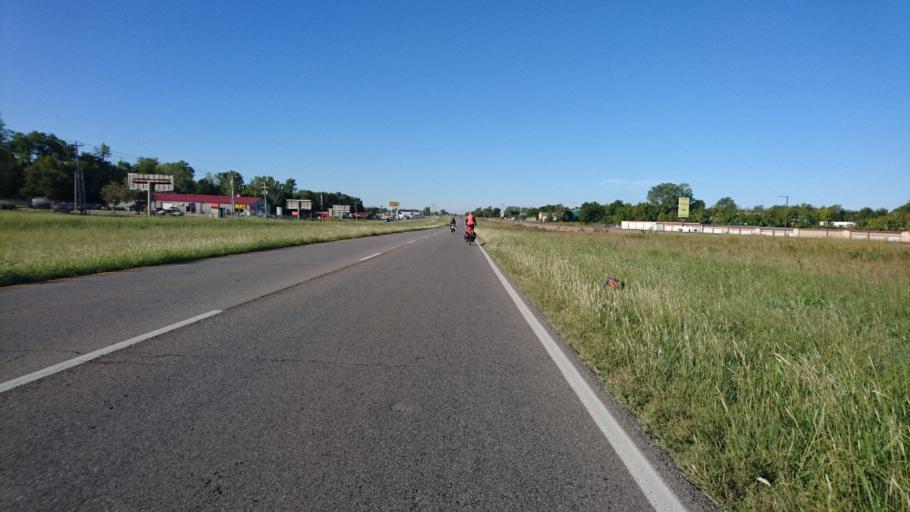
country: US
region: Oklahoma
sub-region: Rogers County
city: Verdigris
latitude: 36.2626
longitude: -95.6548
